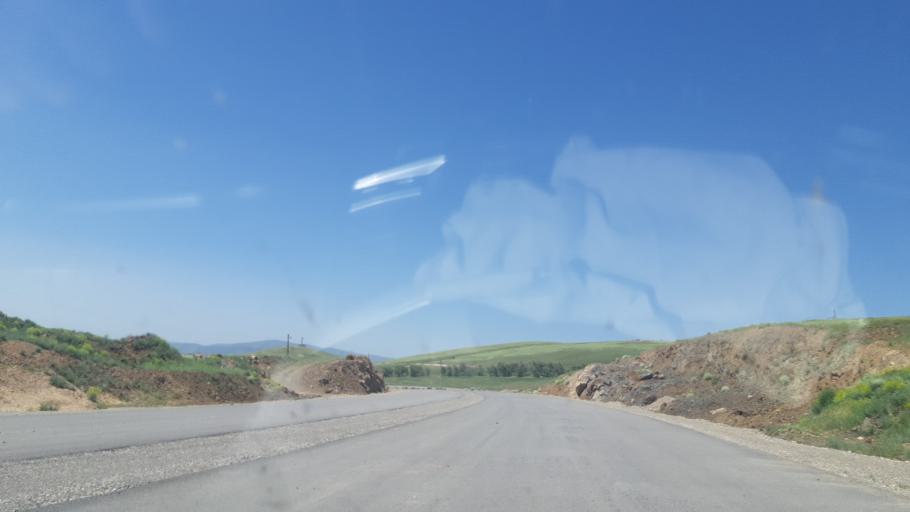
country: KZ
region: Ongtustik Qazaqstan
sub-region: Tulkibas Audany
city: Zhabagly
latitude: 42.5179
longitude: 70.5393
